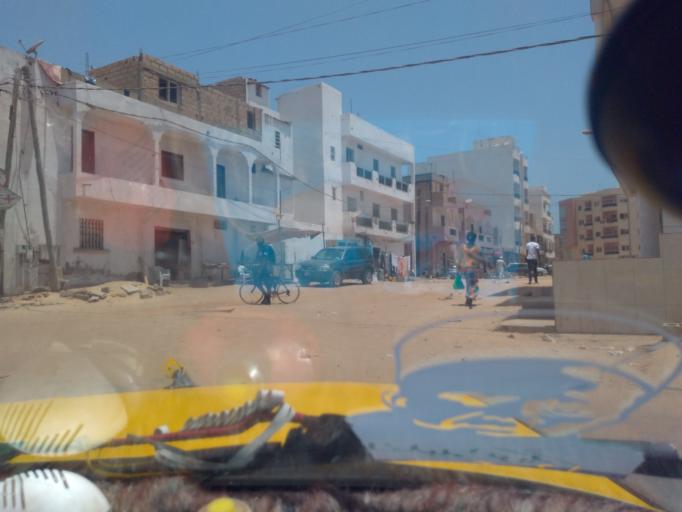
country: SN
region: Dakar
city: Grand Dakar
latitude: 14.7598
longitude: -17.4660
